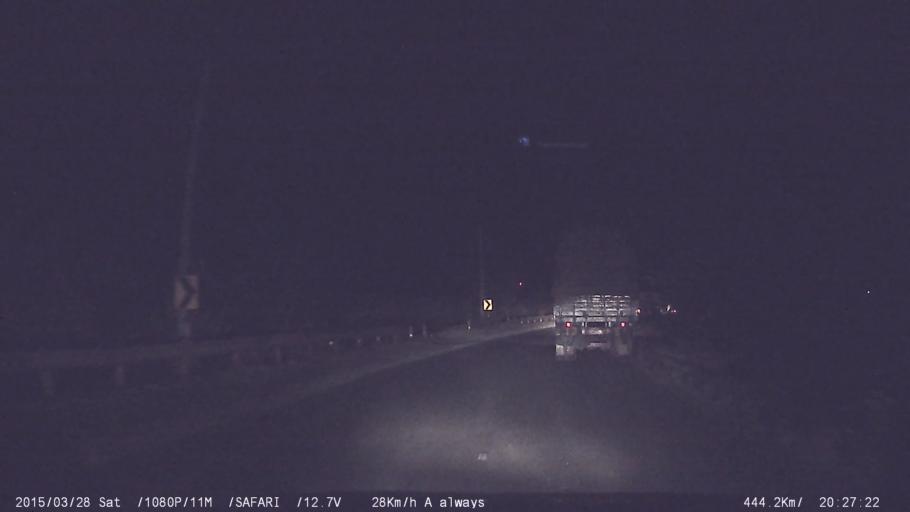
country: IN
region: Karnataka
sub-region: Mandya
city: Maddur
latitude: 12.6113
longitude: 77.0537
